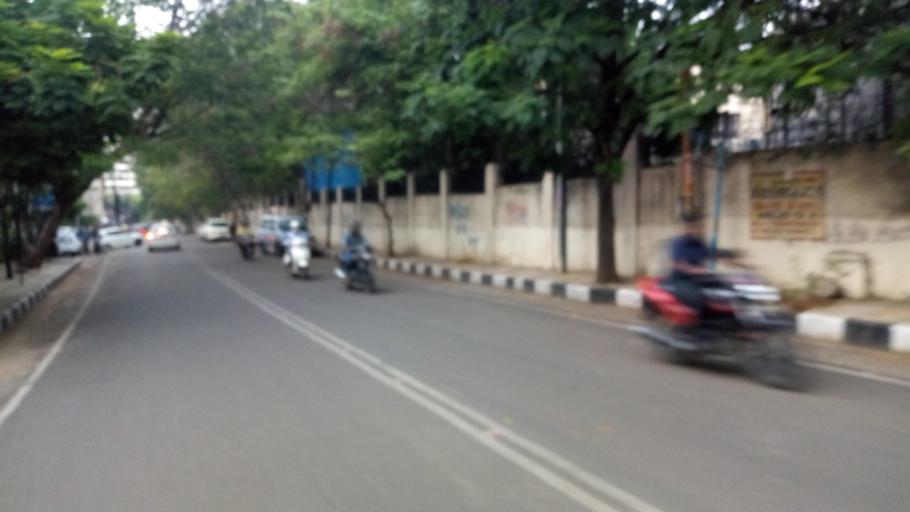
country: IN
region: Telangana
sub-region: Hyderabad
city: Hyderabad
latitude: 17.4045
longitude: 78.4725
